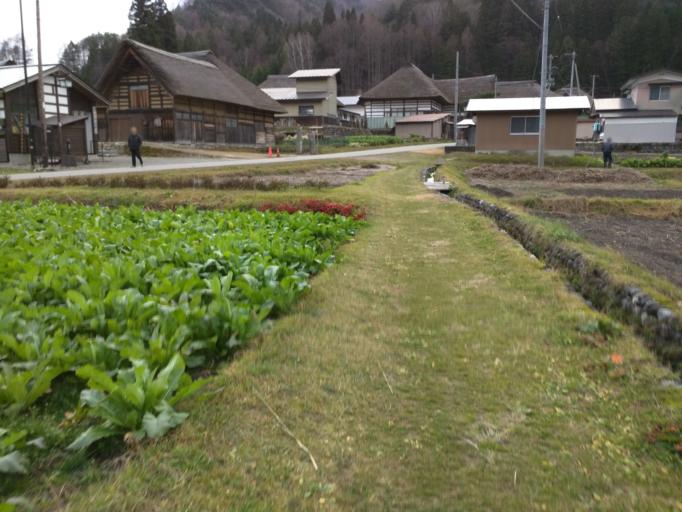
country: JP
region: Tochigi
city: Nikko
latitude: 37.1028
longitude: 139.5209
